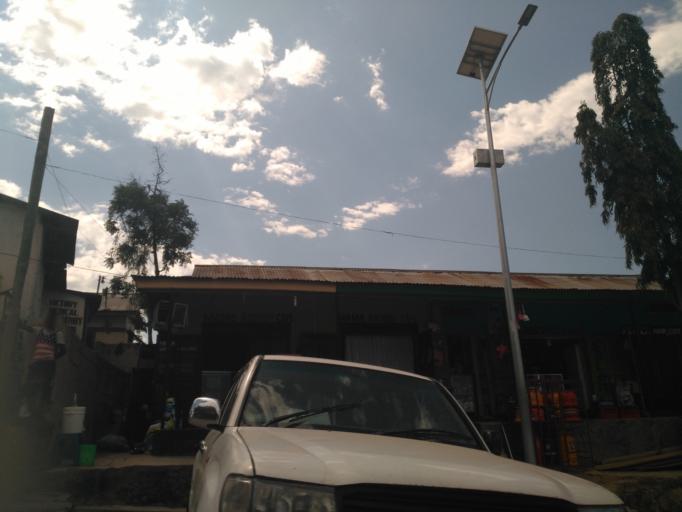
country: TZ
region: Mwanza
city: Mwanza
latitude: -2.5009
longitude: 32.9123
